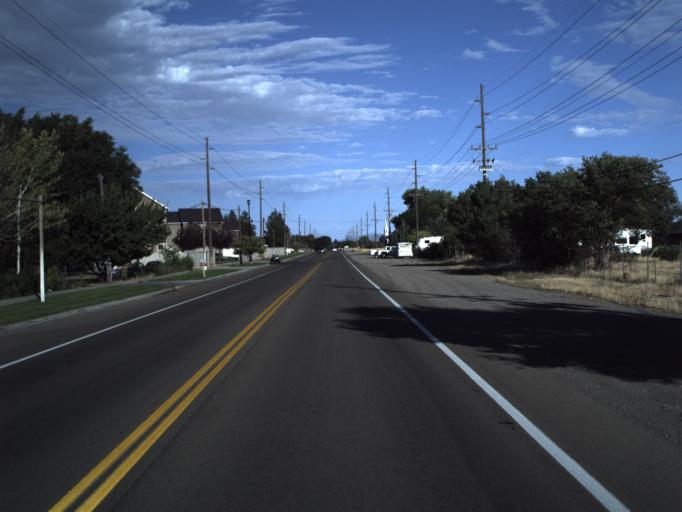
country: US
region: Utah
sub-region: Utah County
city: Spanish Fork
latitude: 40.0977
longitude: -111.6219
